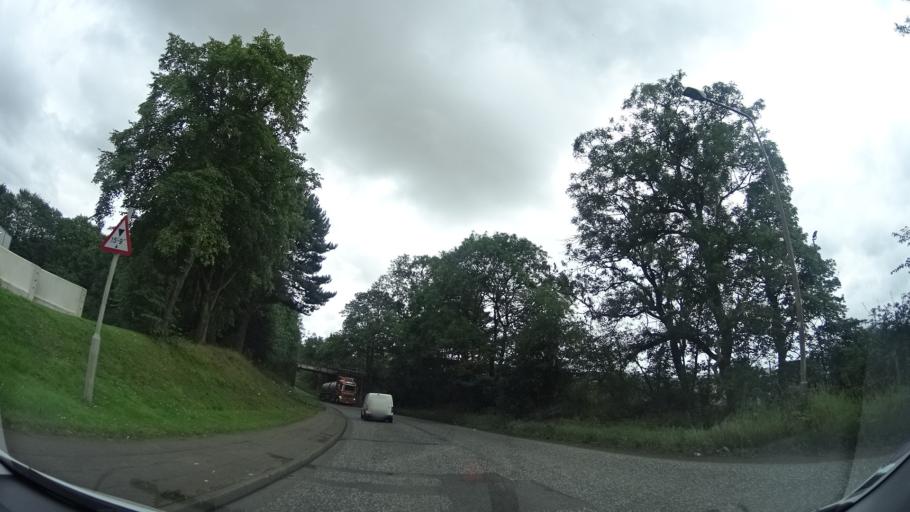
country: GB
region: Scotland
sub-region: Edinburgh
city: Newbridge
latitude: 55.9302
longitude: -3.4157
